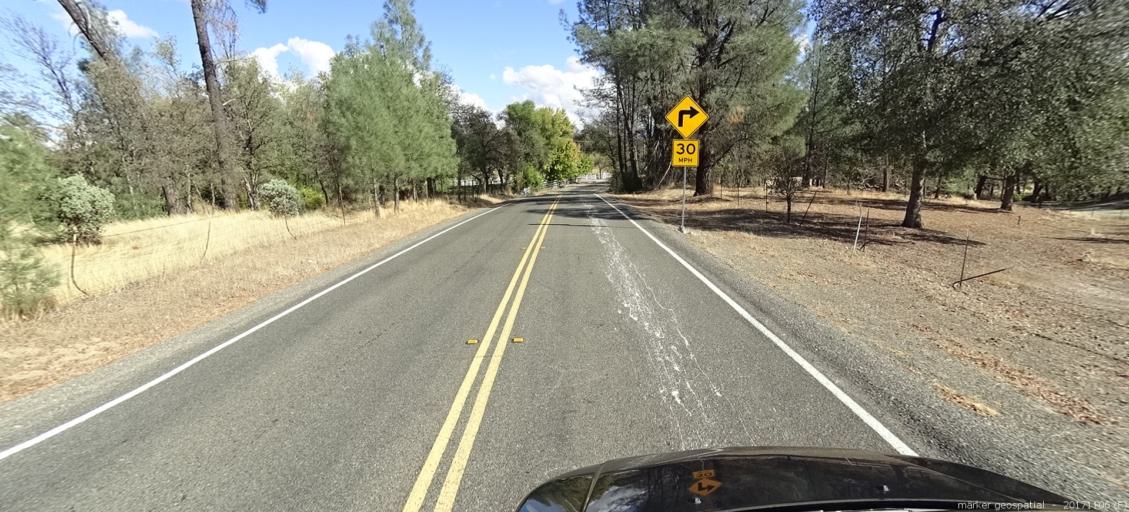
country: US
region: California
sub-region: Shasta County
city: Palo Cedro
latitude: 40.5922
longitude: -122.2440
